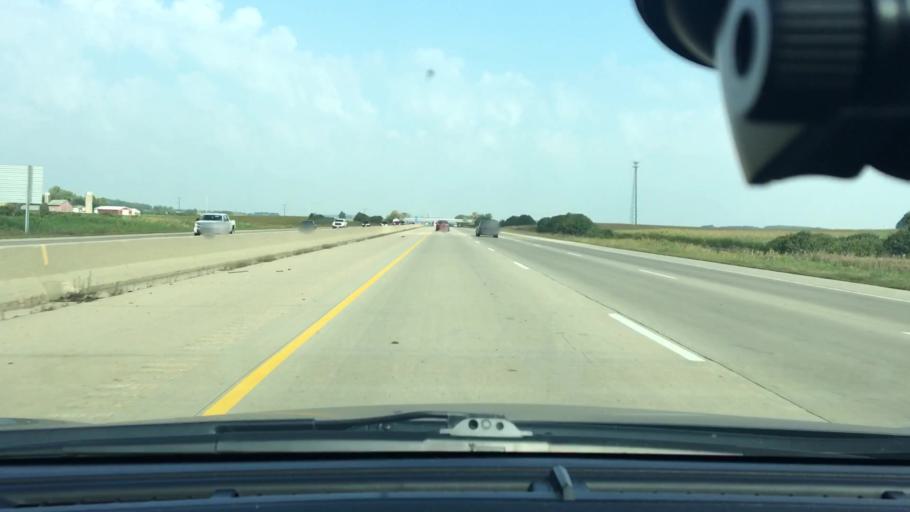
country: US
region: Wisconsin
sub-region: Dane County
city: De Forest
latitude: 43.2694
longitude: -89.3930
